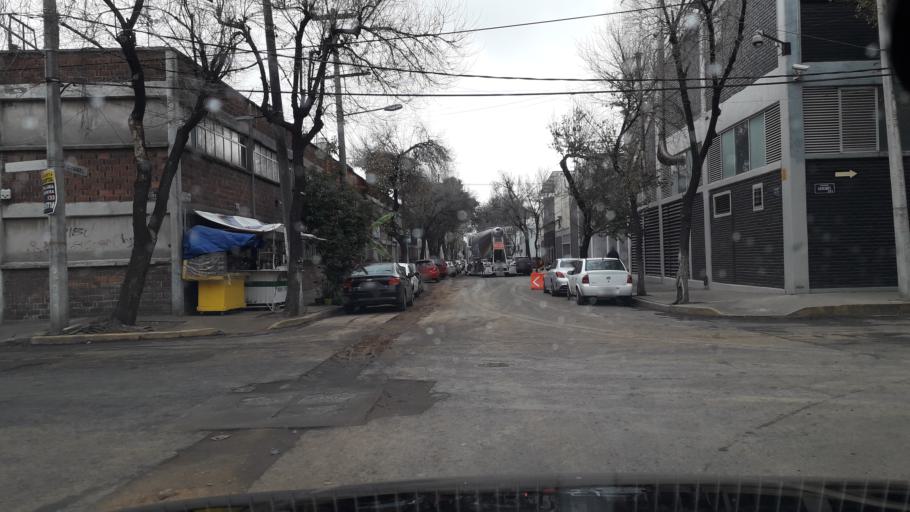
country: MX
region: Mexico City
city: Cuauhtemoc
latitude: 19.4618
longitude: -99.1509
